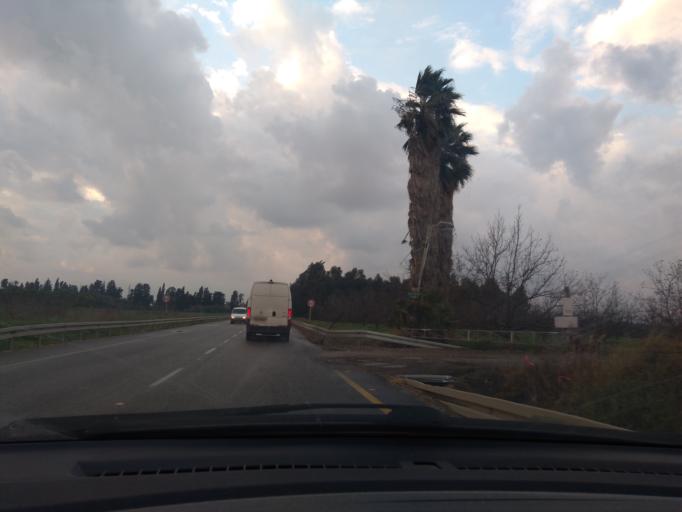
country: IL
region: Central District
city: Elyakhin
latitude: 32.3759
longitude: 34.8999
